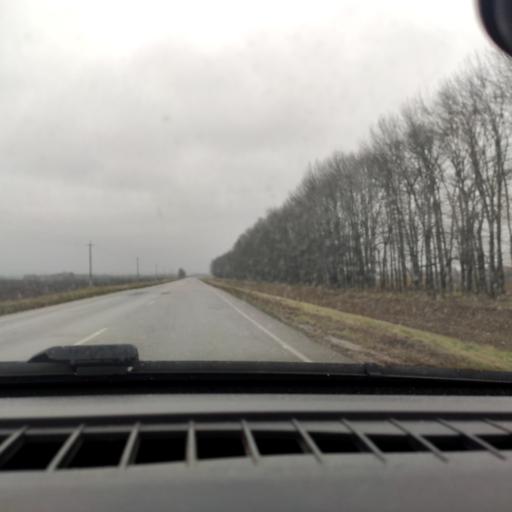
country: RU
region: Belgorod
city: Ilovka
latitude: 50.7470
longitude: 38.7130
